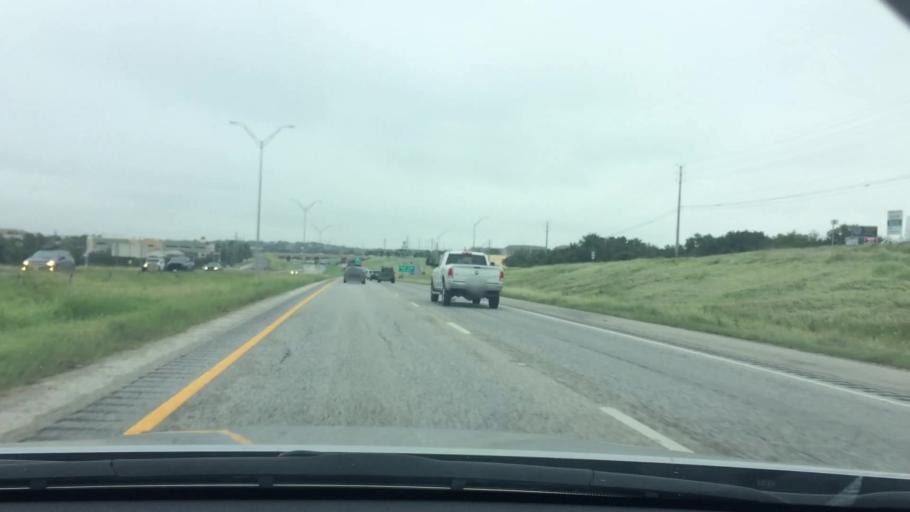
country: US
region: Texas
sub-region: Bexar County
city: Leon Valley
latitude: 29.4563
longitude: -98.6884
